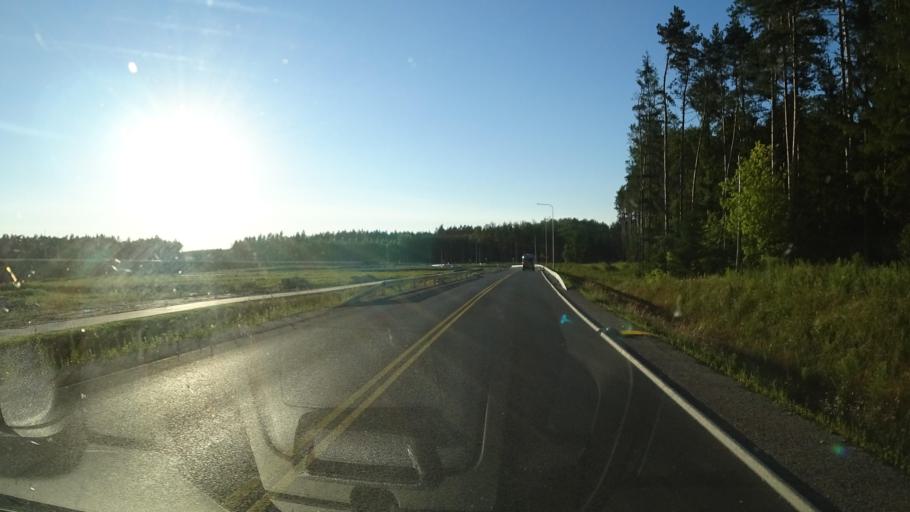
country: PL
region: Warmian-Masurian Voivodeship
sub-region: Powiat elcki
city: Elk
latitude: 53.8387
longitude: 22.4209
